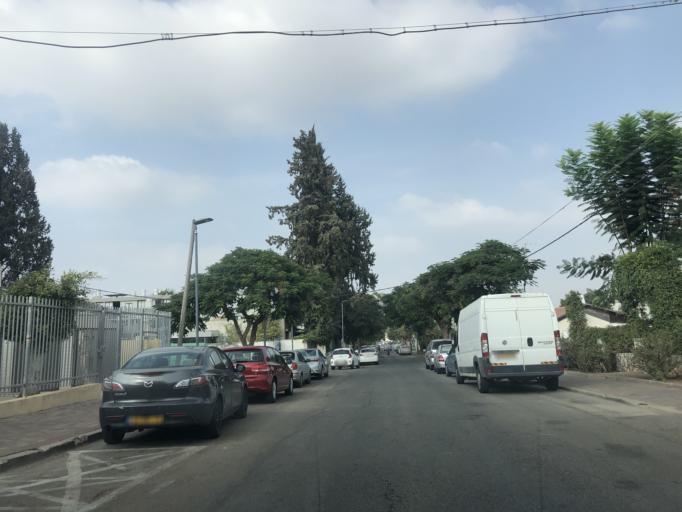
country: IL
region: Central District
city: Rosh Ha'Ayin
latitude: 32.0958
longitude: 34.9525
